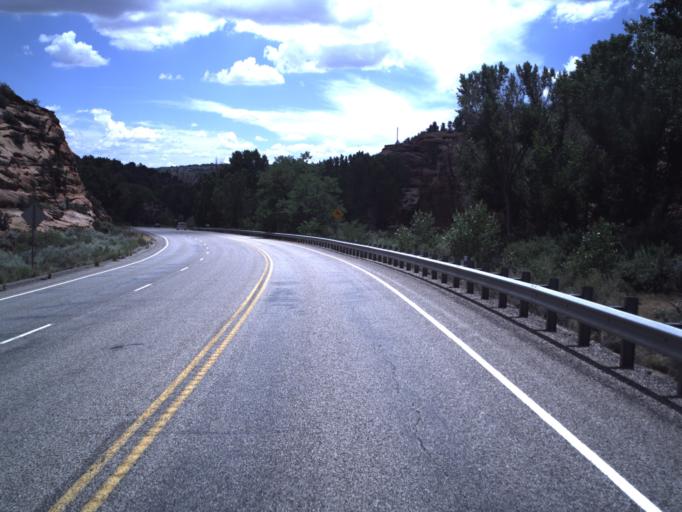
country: US
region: Utah
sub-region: Kane County
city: Kanab
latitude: 37.1340
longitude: -112.5664
